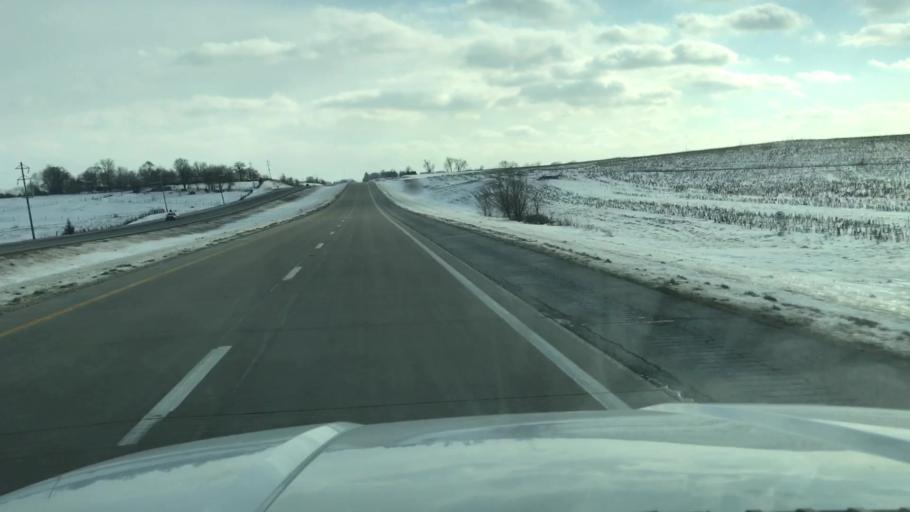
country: US
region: Missouri
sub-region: Nodaway County
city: Maryville
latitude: 40.2237
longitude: -94.8682
